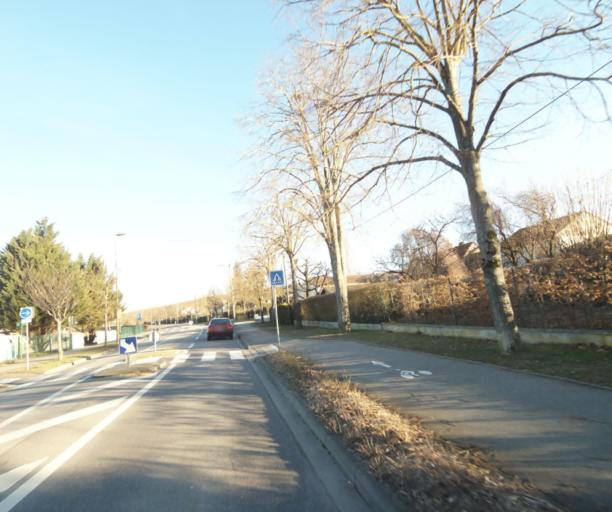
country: FR
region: Lorraine
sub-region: Departement de Meurthe-et-Moselle
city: Pulnoy
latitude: 48.7049
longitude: 6.2635
